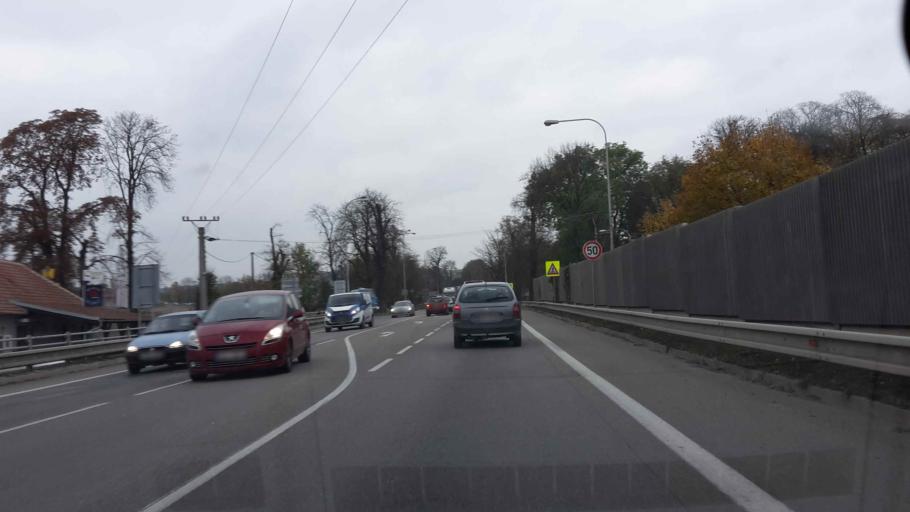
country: CZ
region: South Moravian
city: Slavkov u Brna
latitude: 49.1523
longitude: 16.8656
